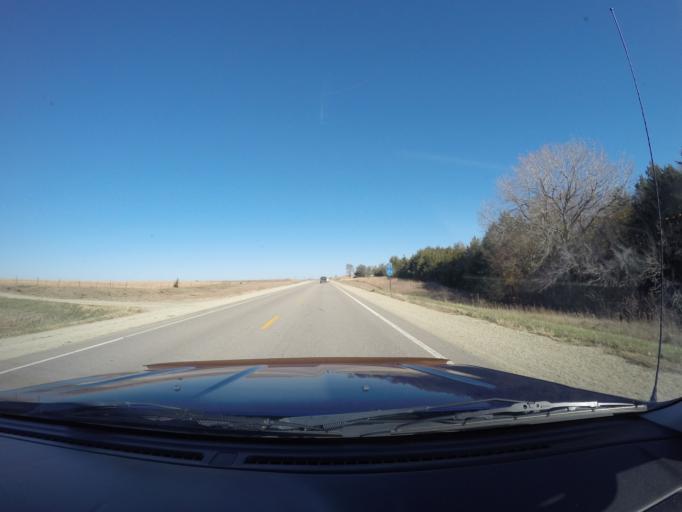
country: US
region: Kansas
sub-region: Riley County
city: Ogden
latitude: 39.3331
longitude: -96.7561
